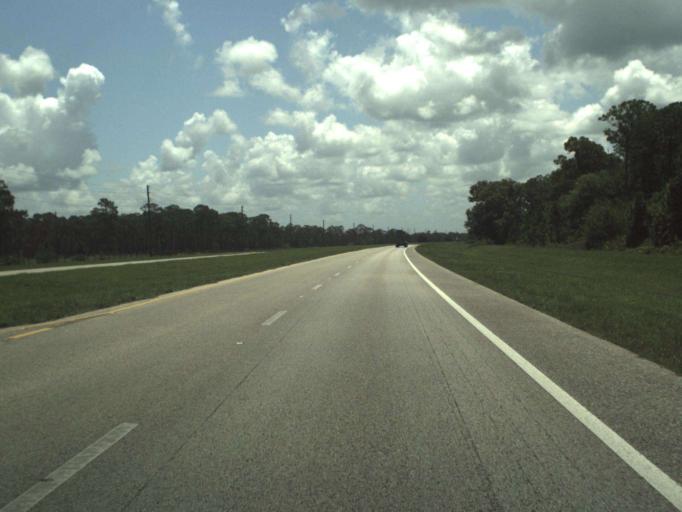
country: US
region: Florida
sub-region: Indian River County
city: Fellsmere
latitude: 27.6803
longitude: -80.8261
